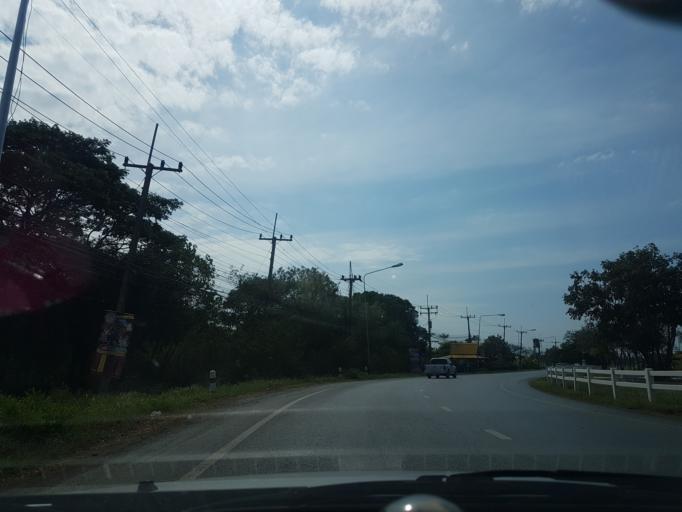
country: TH
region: Lop Buri
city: Lop Buri
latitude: 14.7975
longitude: 100.7142
